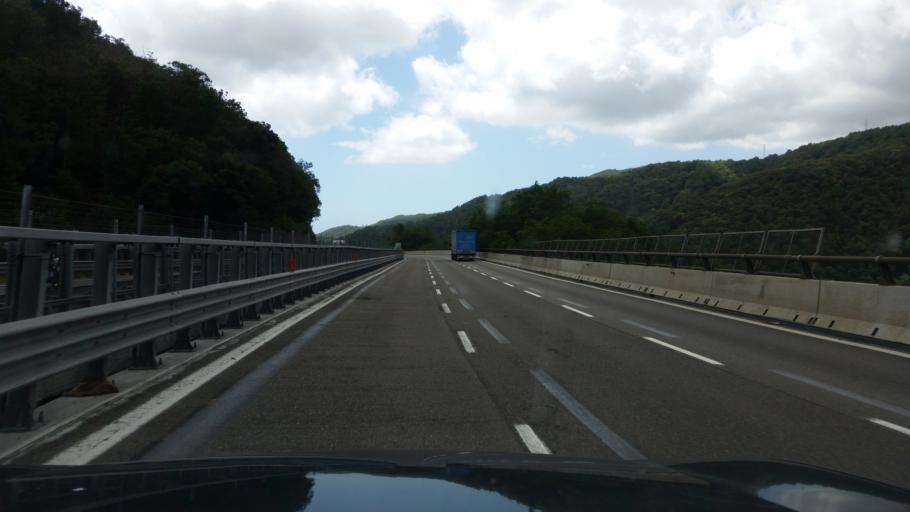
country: IT
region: Liguria
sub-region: Provincia di Genova
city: Masone
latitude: 44.4777
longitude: 8.7354
